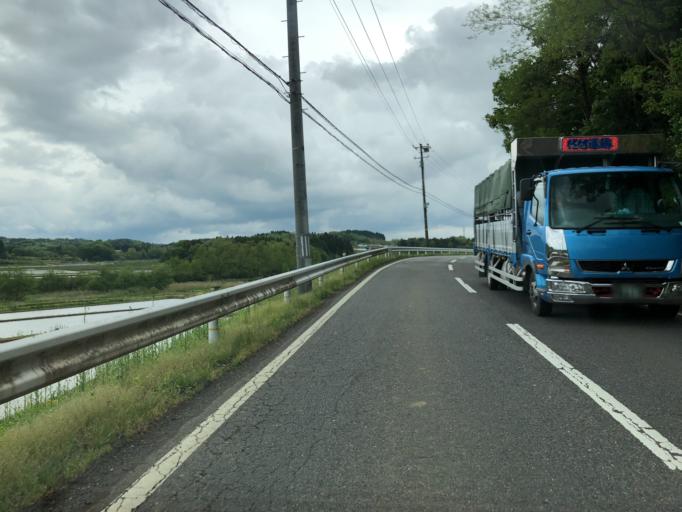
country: JP
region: Fukushima
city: Ishikawa
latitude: 37.1837
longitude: 140.4035
